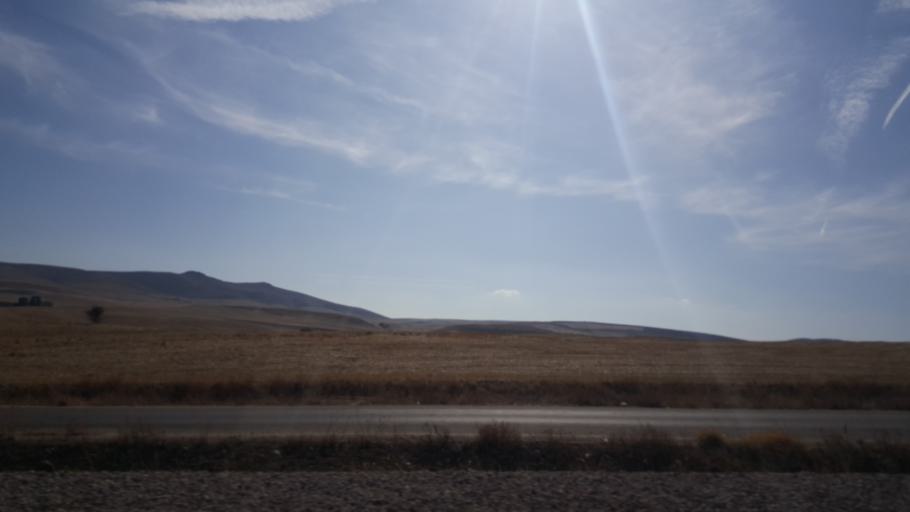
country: TR
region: Ankara
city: Yenice
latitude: 39.3649
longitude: 32.6807
